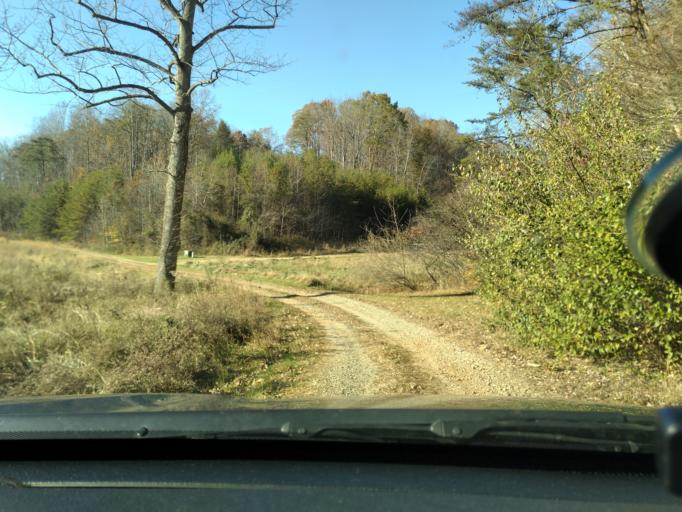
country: US
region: Virginia
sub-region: Floyd County
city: Floyd
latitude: 36.8337
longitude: -80.1799
